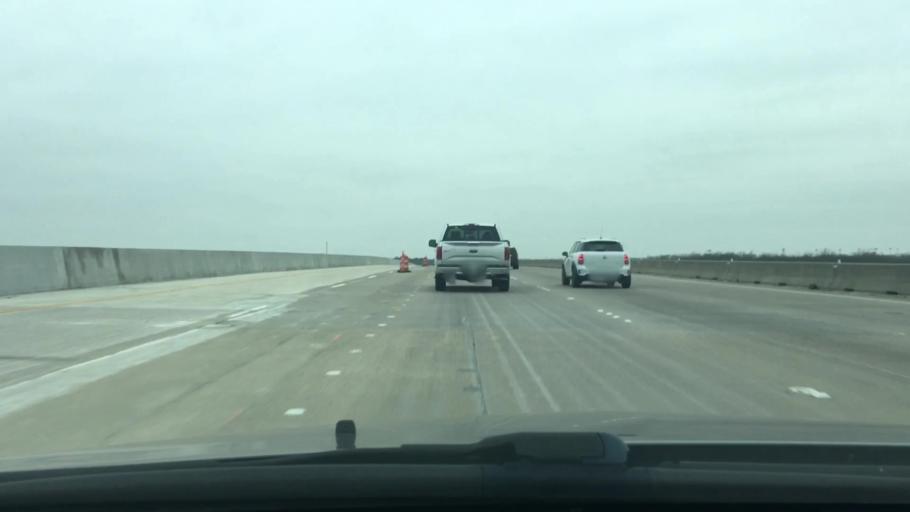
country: US
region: Texas
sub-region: Navarro County
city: Corsicana
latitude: 32.0956
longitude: -96.4407
